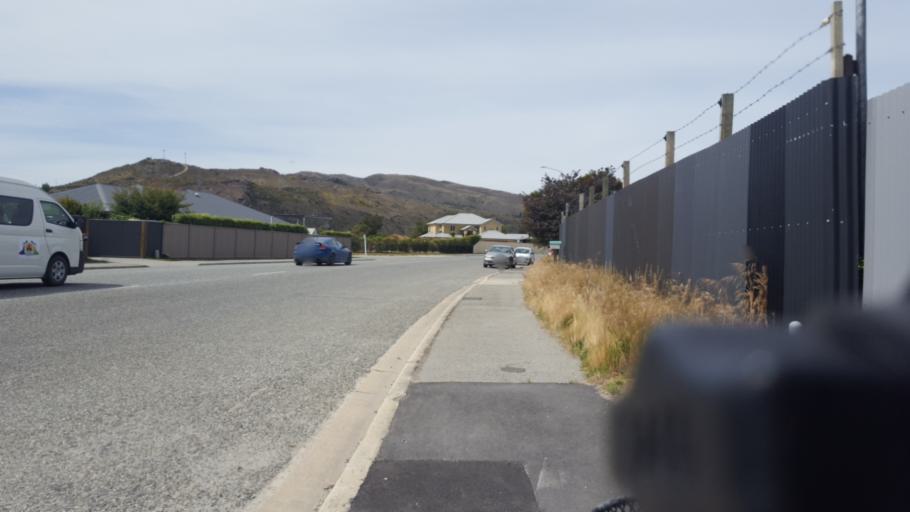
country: NZ
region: Otago
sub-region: Queenstown-Lakes District
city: Wanaka
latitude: -45.0513
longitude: 169.1956
